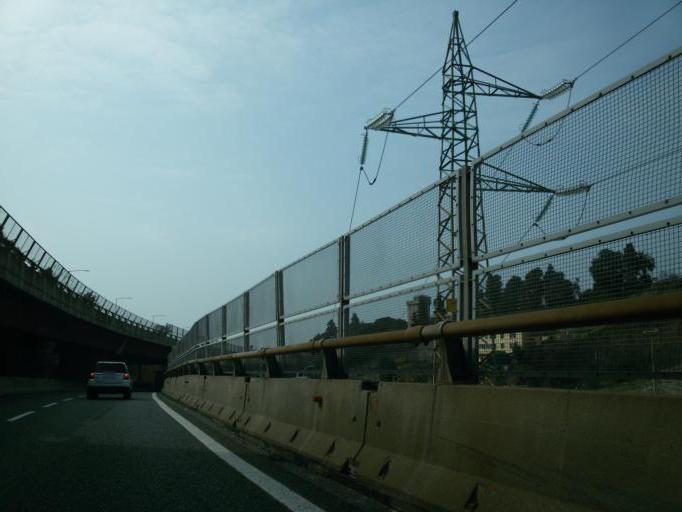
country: IT
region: Liguria
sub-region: Provincia di Genova
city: San Teodoro
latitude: 44.4176
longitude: 8.8648
